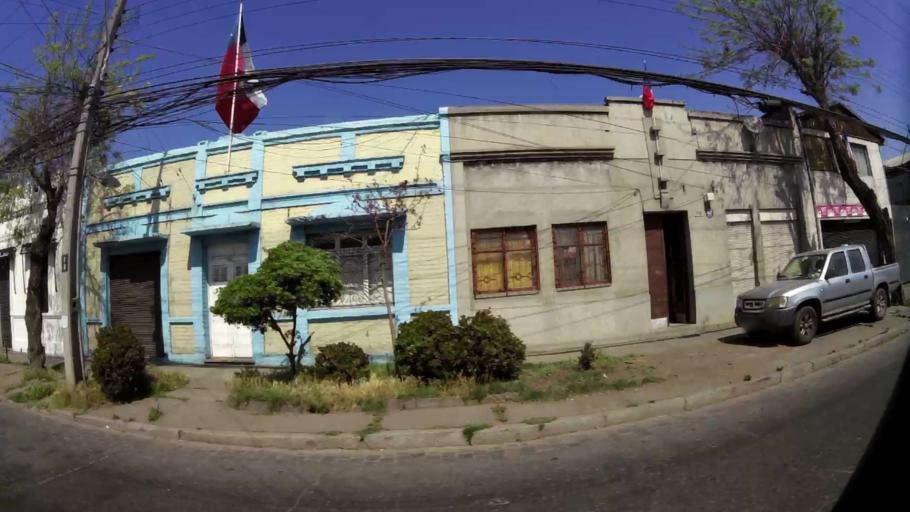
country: CL
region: Santiago Metropolitan
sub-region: Provincia de Santiago
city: Santiago
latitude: -33.4667
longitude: -70.6763
